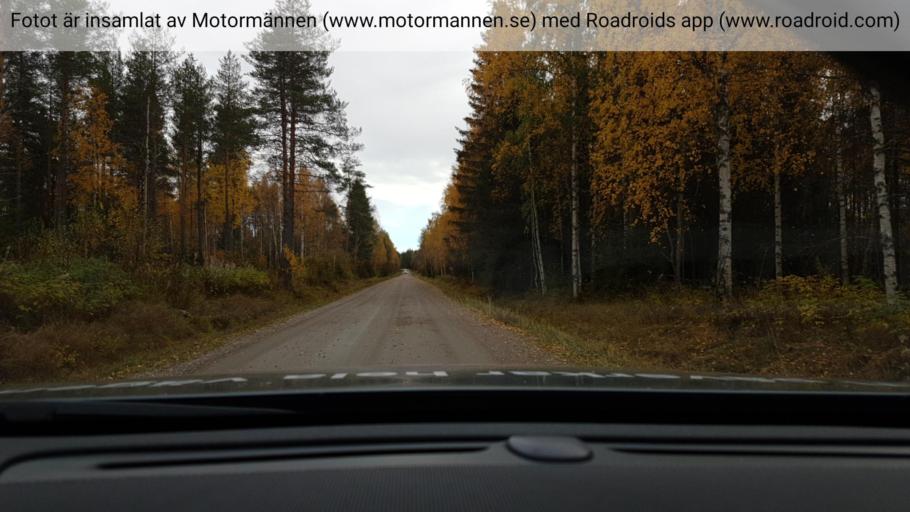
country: SE
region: Norrbotten
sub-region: Overkalix Kommun
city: OEverkalix
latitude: 66.2955
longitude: 22.9446
